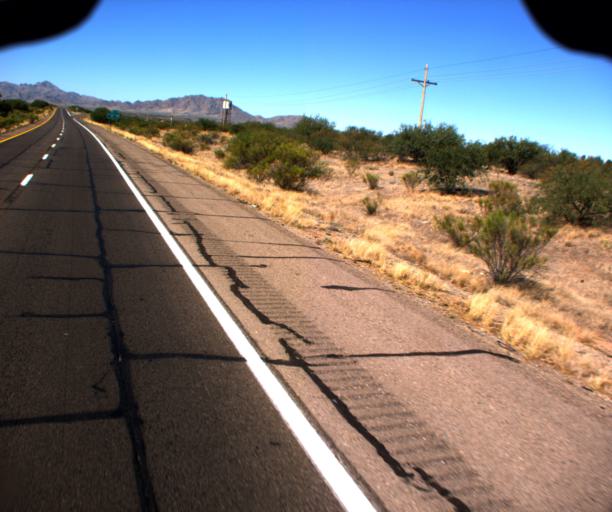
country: US
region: Arizona
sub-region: Pima County
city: Arivaca Junction
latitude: 31.7323
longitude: -111.0553
